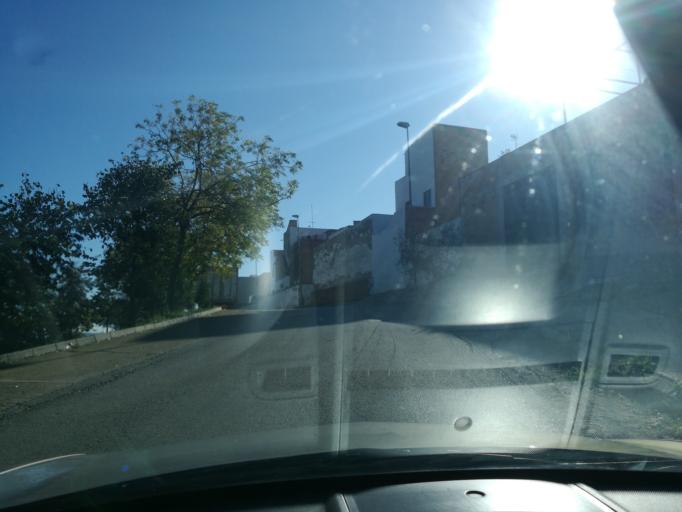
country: ES
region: Andalusia
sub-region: Provincia de Sevilla
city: La Campana
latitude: 37.5706
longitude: -5.4231
